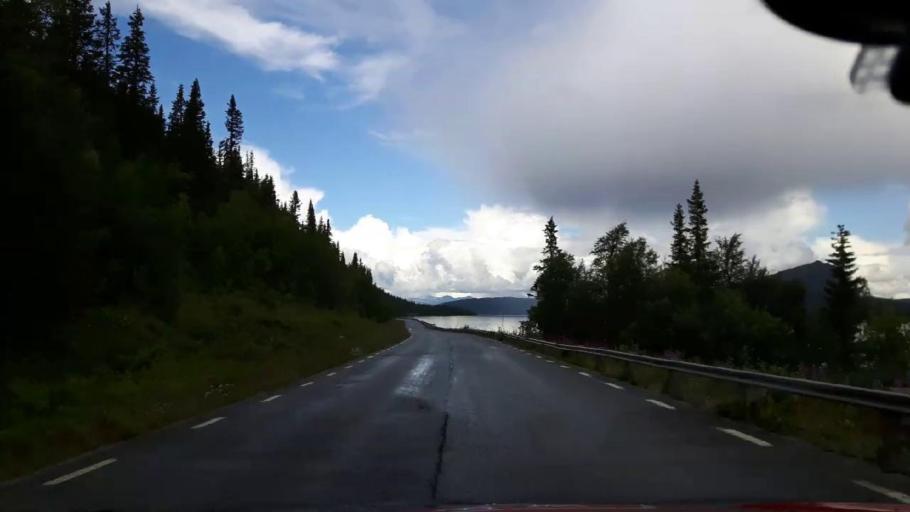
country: SE
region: Vaesterbotten
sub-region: Vilhelmina Kommun
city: Sjoberg
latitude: 64.9782
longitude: 15.3160
